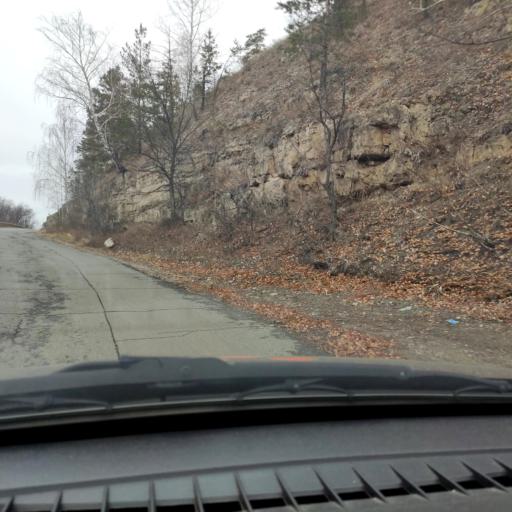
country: RU
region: Samara
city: Povolzhskiy
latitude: 53.4333
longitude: 49.6718
